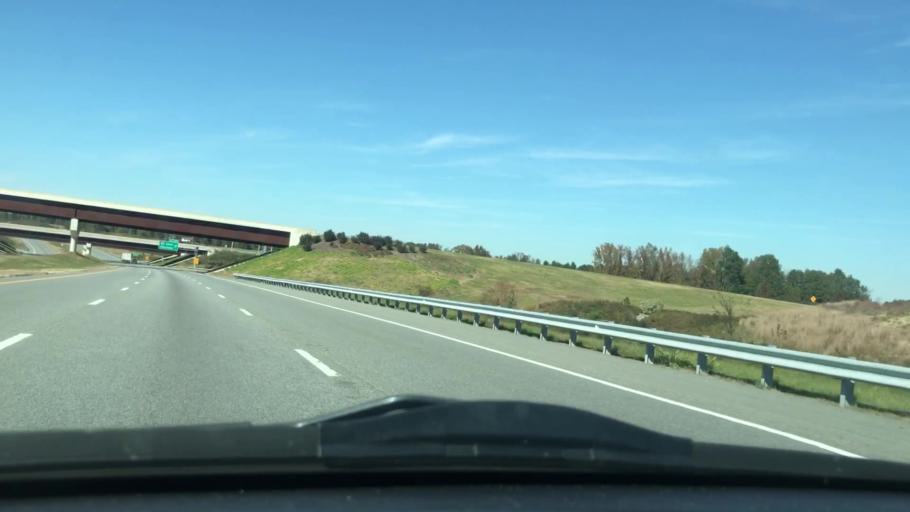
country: US
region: North Carolina
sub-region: Randolph County
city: Archdale
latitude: 35.9263
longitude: -79.9223
